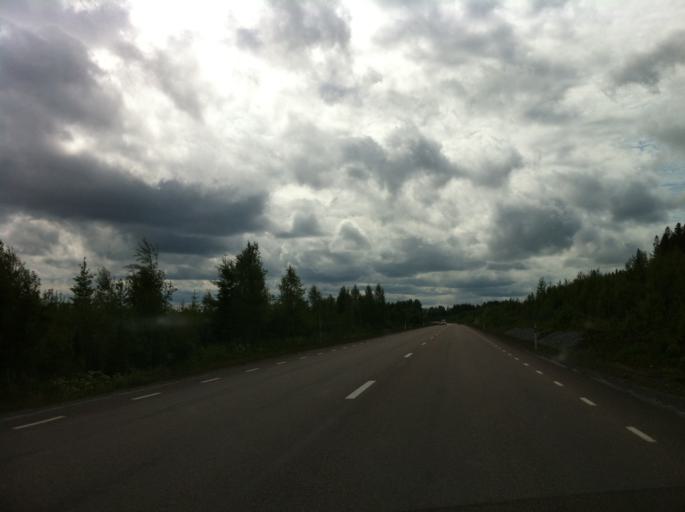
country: SE
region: Vaermland
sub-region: Sunne Kommun
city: Sunne
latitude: 59.7518
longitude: 13.1198
